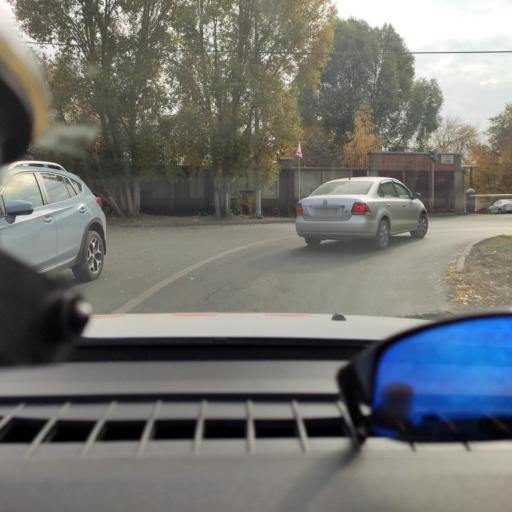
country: RU
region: Samara
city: Samara
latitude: 53.2387
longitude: 50.1965
